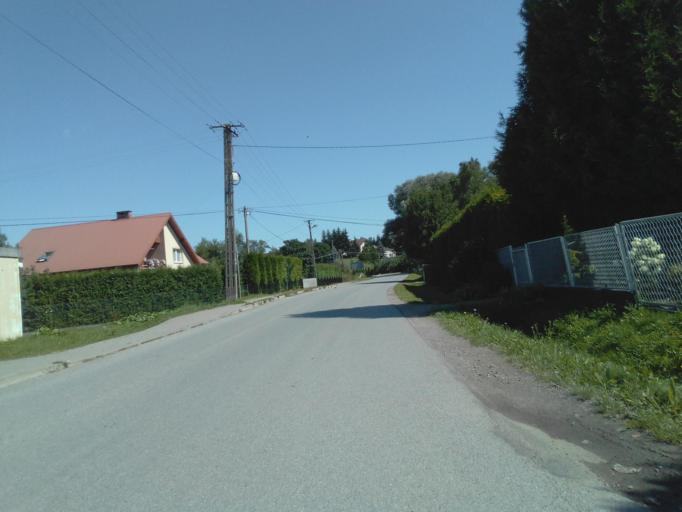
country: PL
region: Subcarpathian Voivodeship
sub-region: Powiat krosnienski
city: Chorkowka
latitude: 49.6657
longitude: 21.6111
